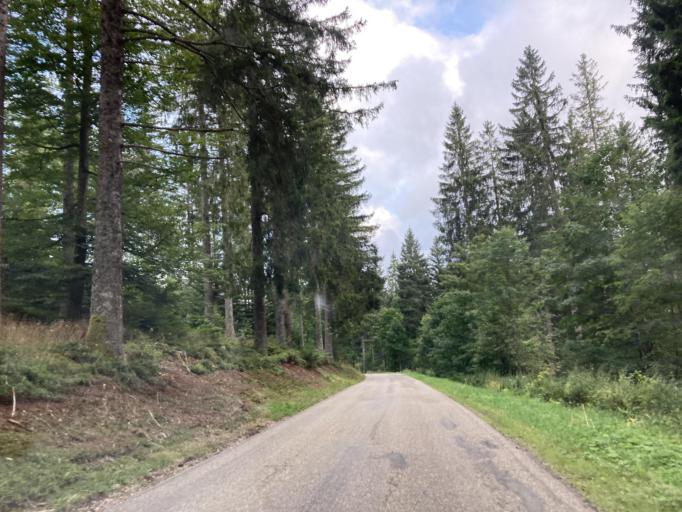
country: DE
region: Baden-Wuerttemberg
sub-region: Freiburg Region
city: Furtwangen im Schwarzwald
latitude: 48.0605
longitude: 8.1869
